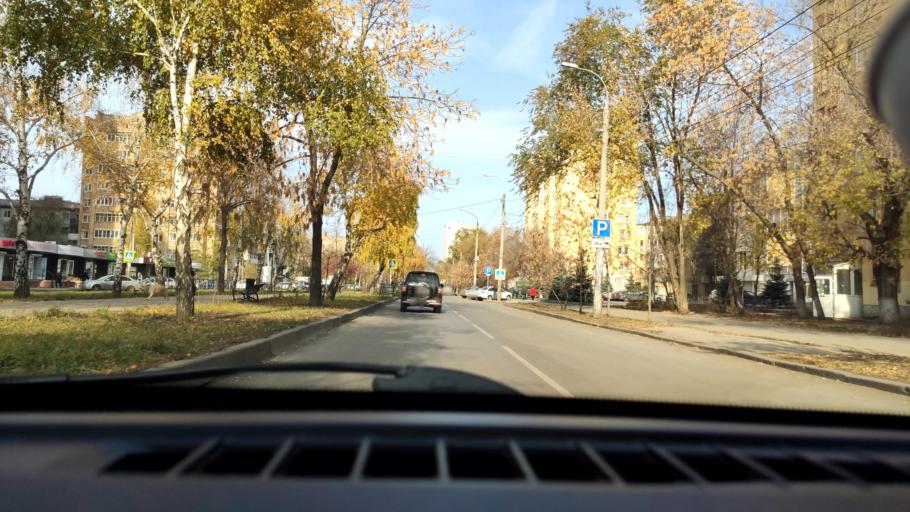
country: RU
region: Samara
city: Samara
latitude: 53.1932
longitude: 50.1790
